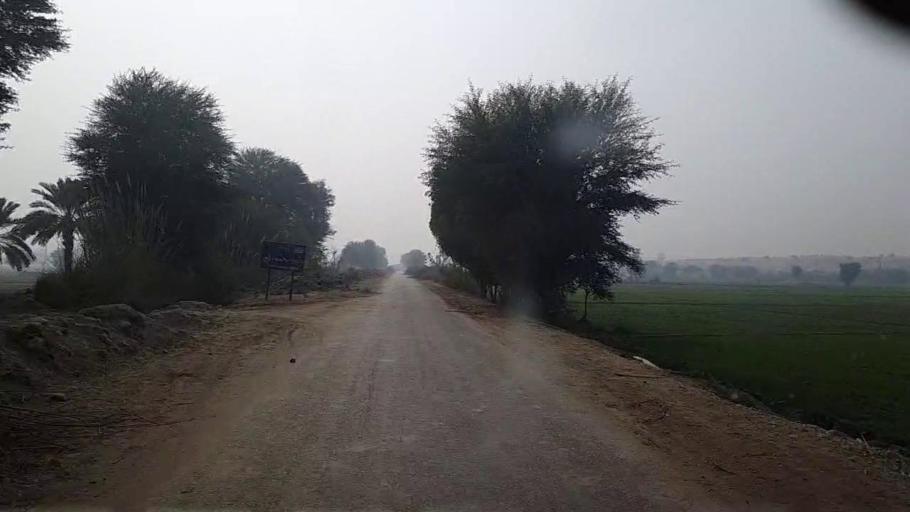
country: PK
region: Sindh
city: Kandiari
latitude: 26.9867
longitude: 68.6035
